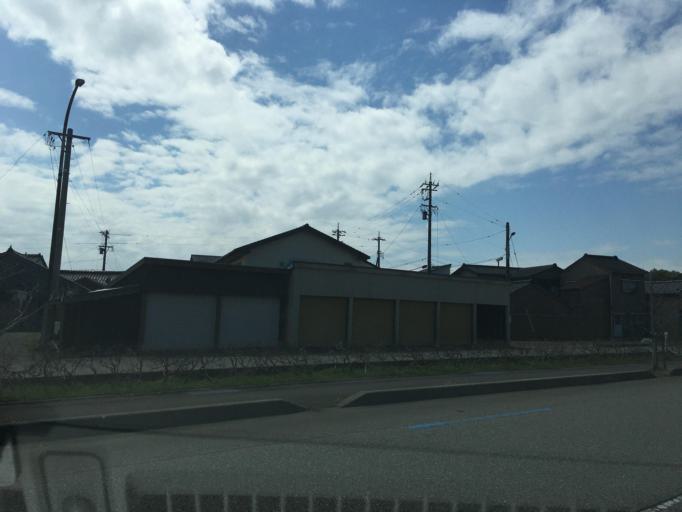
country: JP
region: Toyama
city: Kuragaki-kosugi
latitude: 36.7712
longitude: 137.1299
